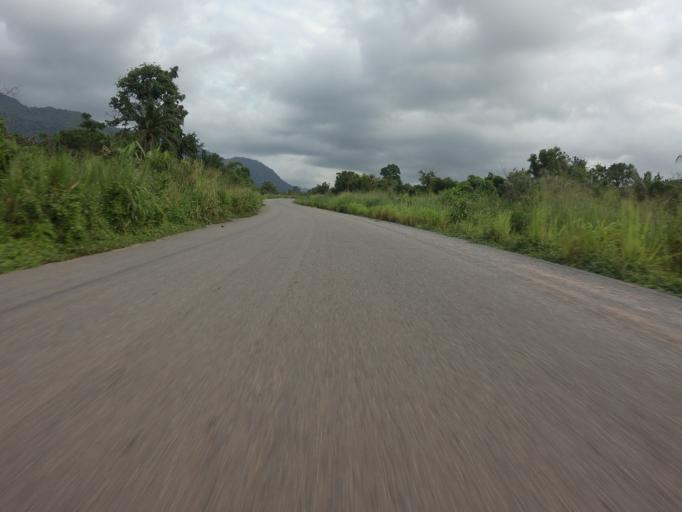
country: GH
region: Volta
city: Kpandu
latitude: 6.8249
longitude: 0.3786
